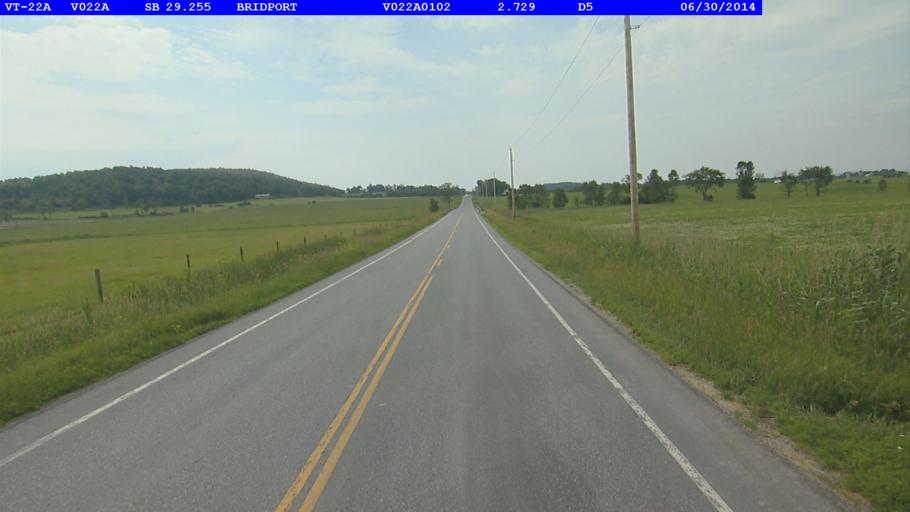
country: US
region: Vermont
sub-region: Addison County
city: Middlebury (village)
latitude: 43.9797
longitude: -73.3124
